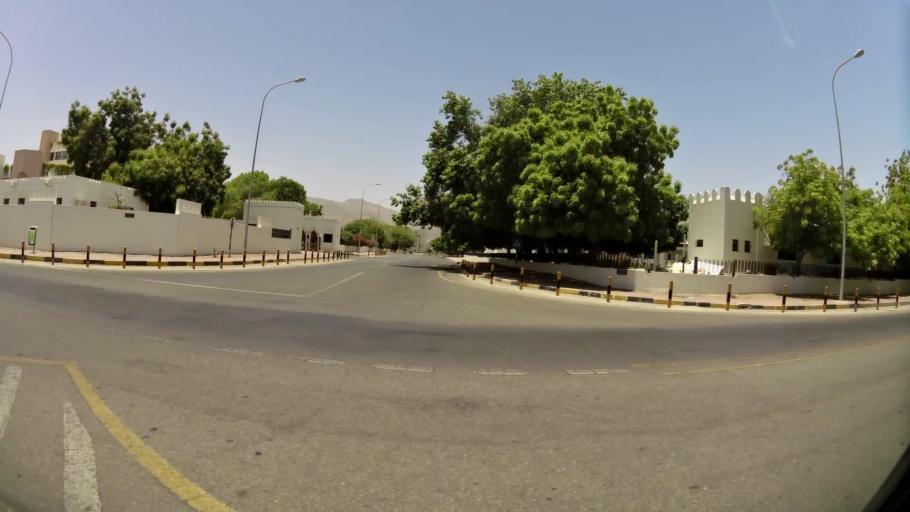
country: OM
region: Muhafazat Masqat
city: Bawshar
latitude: 23.6001
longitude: 58.4362
